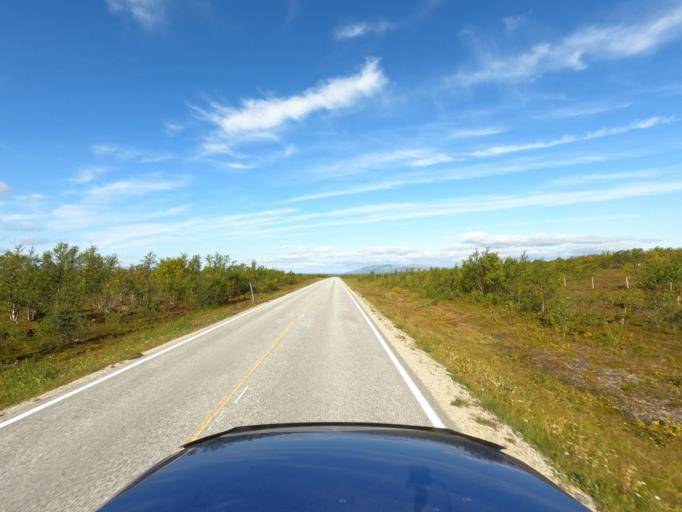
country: NO
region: Finnmark Fylke
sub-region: Karasjok
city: Karasjohka
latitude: 69.7171
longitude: 25.2400
